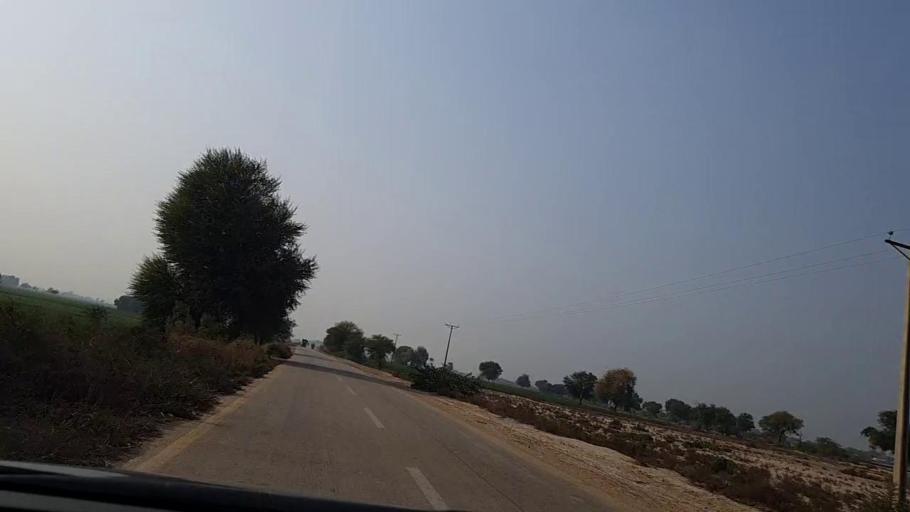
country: PK
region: Sindh
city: Sakrand
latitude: 26.1355
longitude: 68.1906
